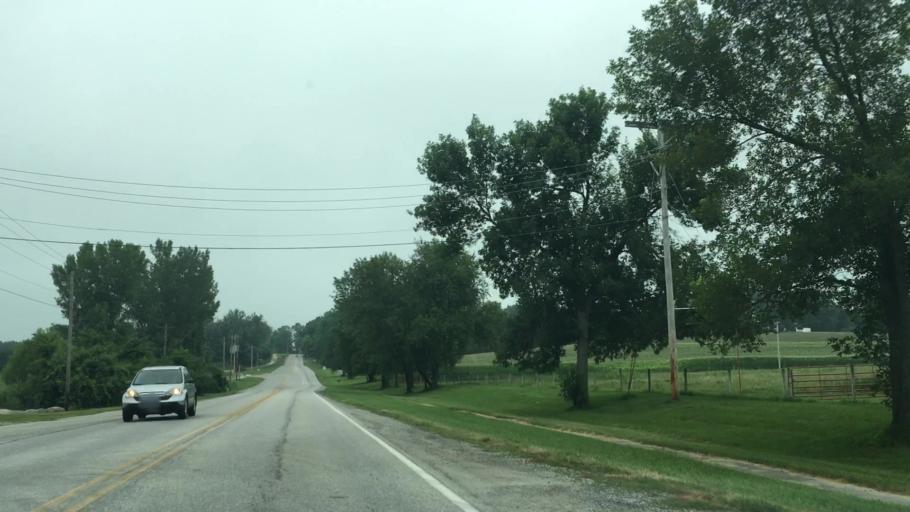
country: US
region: Iowa
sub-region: Johnson County
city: Iowa City
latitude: 41.6965
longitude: -91.5466
